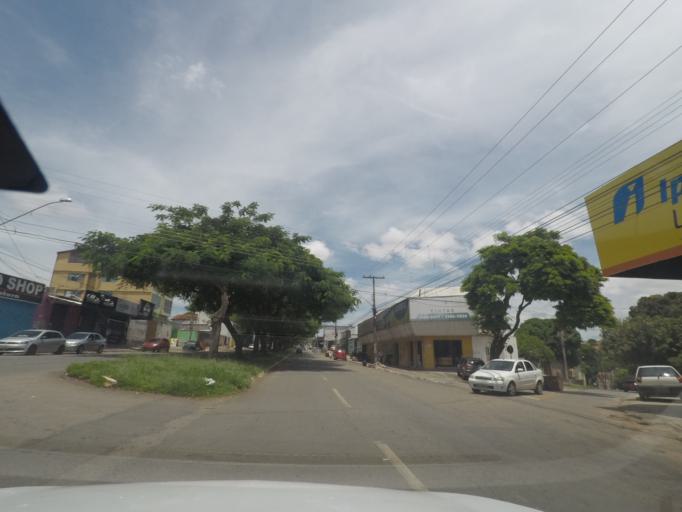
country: BR
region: Goias
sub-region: Goiania
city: Goiania
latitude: -16.6652
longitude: -49.2158
